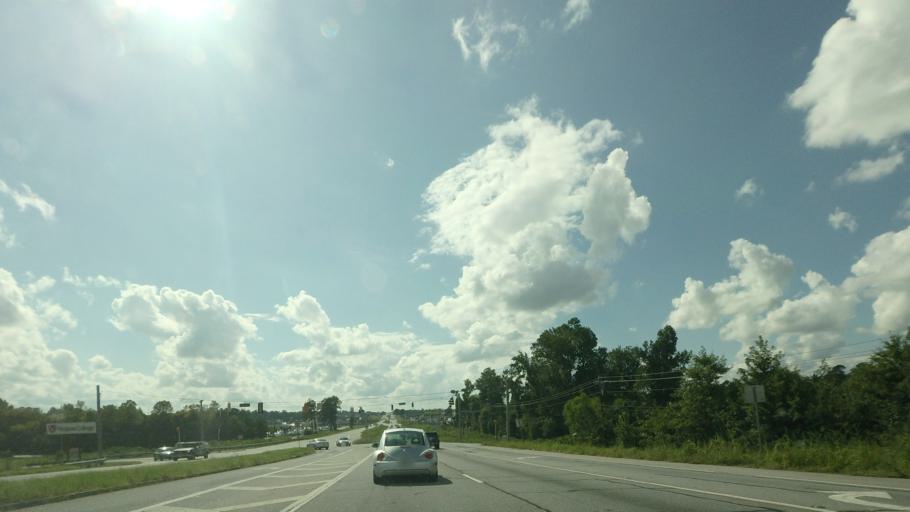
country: US
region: Georgia
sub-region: Bibb County
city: Macon
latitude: 32.8150
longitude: -83.6789
